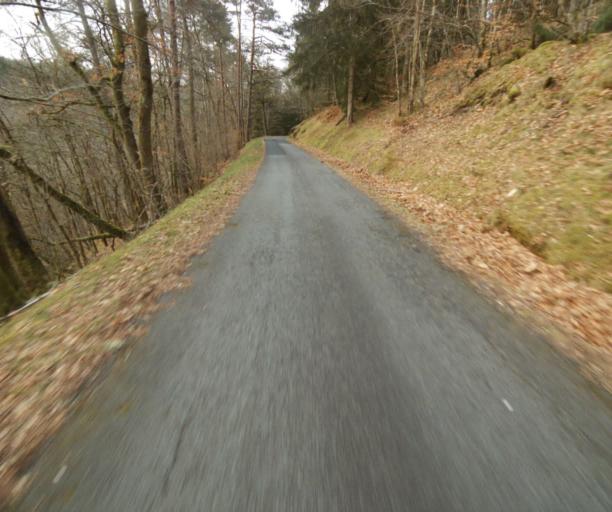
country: FR
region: Limousin
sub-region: Departement de la Correze
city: Correze
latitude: 45.3886
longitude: 1.8891
